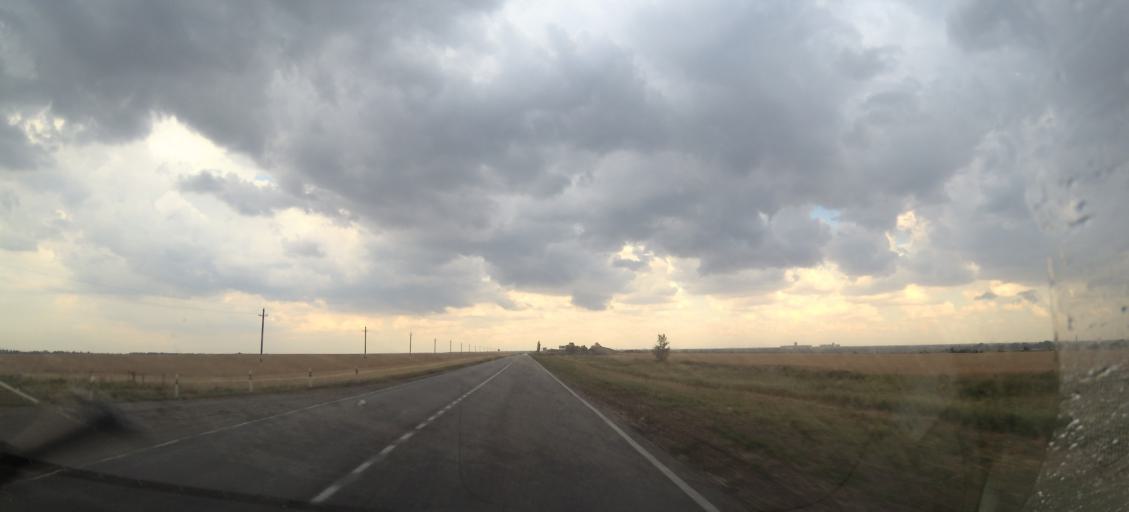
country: RU
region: Rostov
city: Orlovskiy
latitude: 46.8747
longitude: 41.9925
